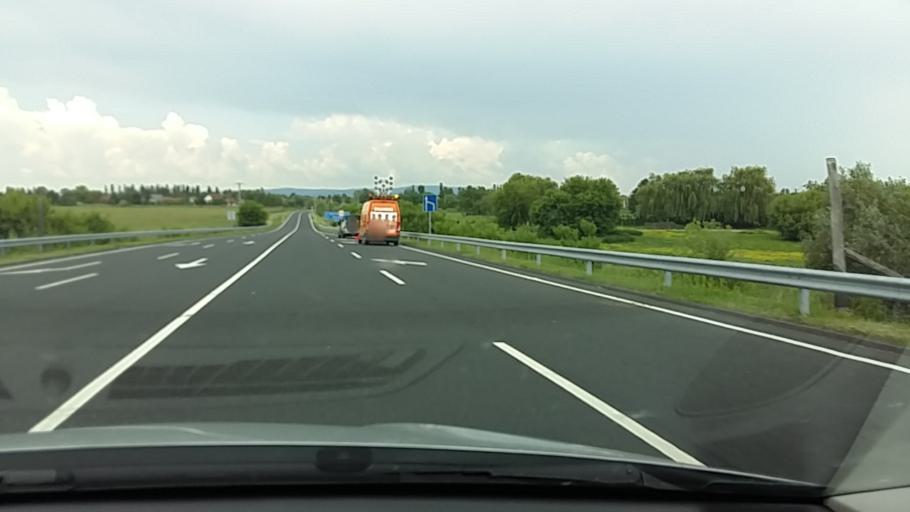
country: HU
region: Somogy
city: Balatonfenyves
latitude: 46.7026
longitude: 17.4711
